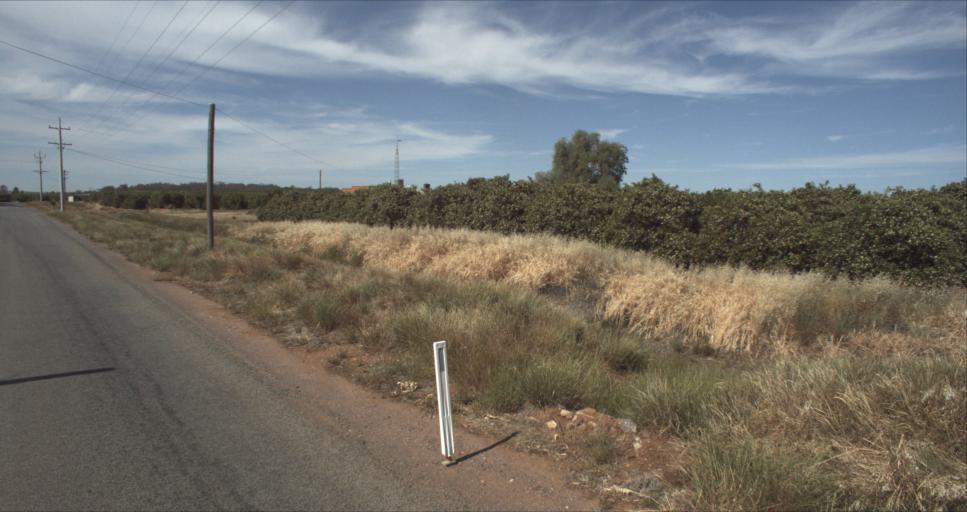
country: AU
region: New South Wales
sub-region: Leeton
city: Leeton
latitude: -34.5862
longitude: 146.4722
